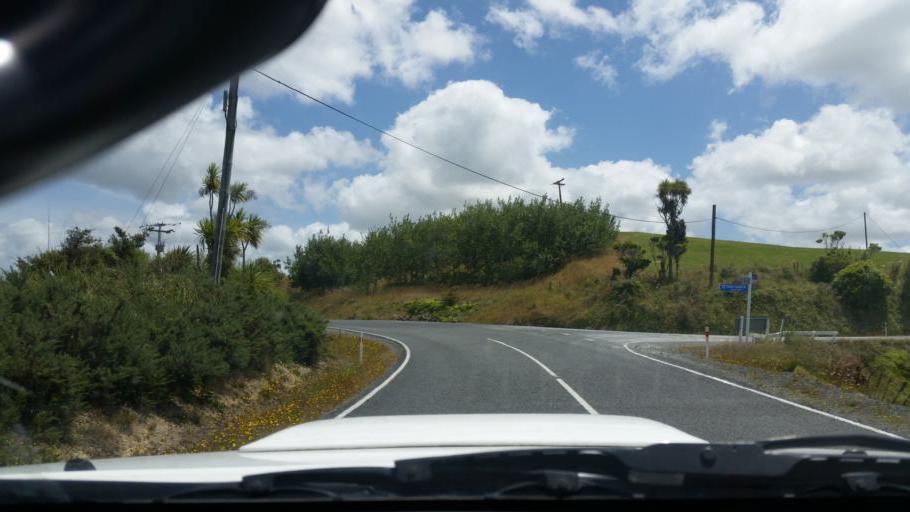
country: NZ
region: Northland
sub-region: Whangarei
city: Ruakaka
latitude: -36.0785
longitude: 174.2418
